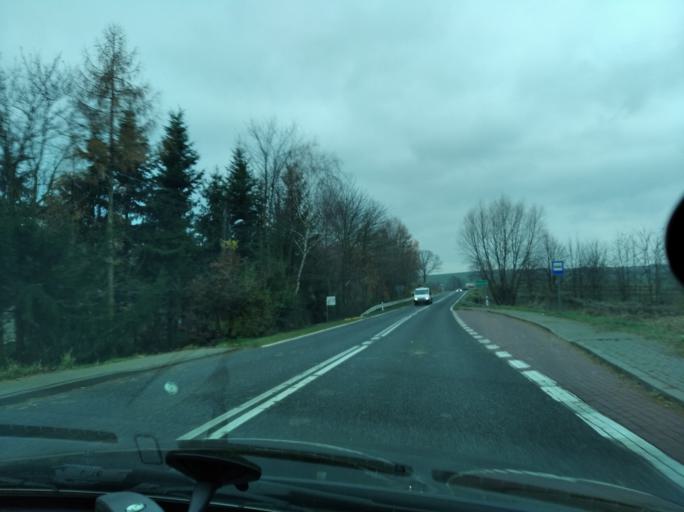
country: PL
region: Subcarpathian Voivodeship
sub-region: Powiat przeworski
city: Kanczuga
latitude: 49.9842
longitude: 22.4001
